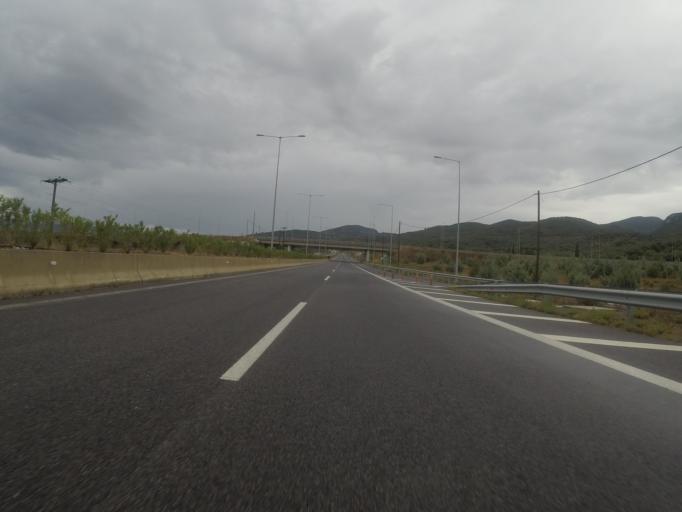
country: GR
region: Peloponnese
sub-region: Nomos Messinias
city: Meligalas
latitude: 37.2480
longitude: 22.0218
